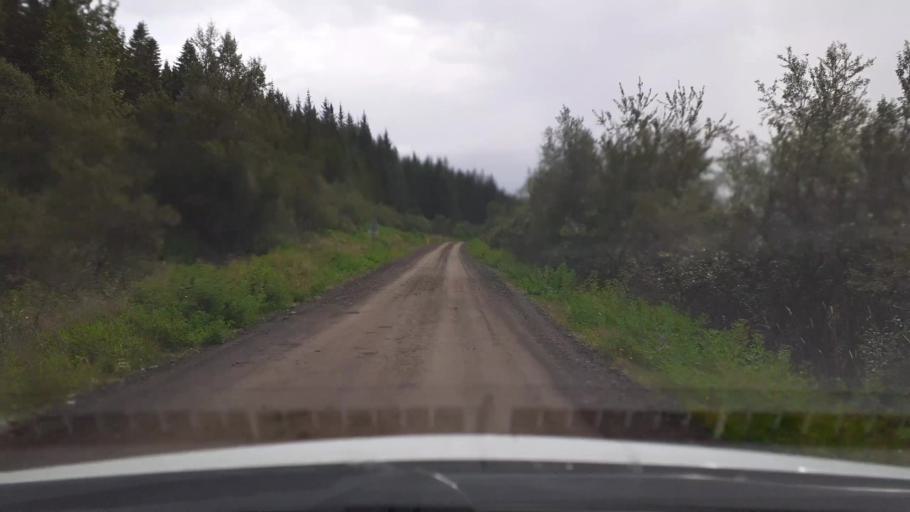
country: IS
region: Capital Region
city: Mosfellsbaer
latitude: 64.5167
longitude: -21.4183
